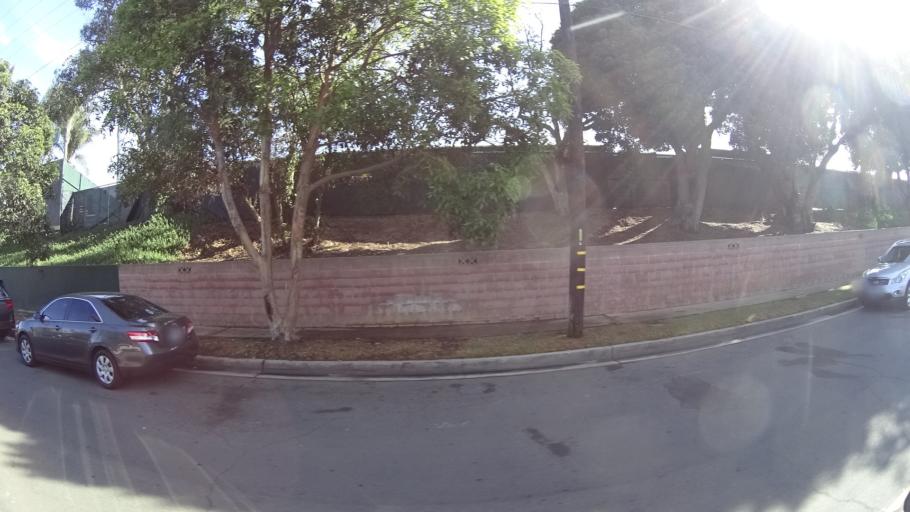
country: US
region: California
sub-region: Los Angeles County
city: Hermosa Beach
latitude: 33.8747
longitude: -118.3917
